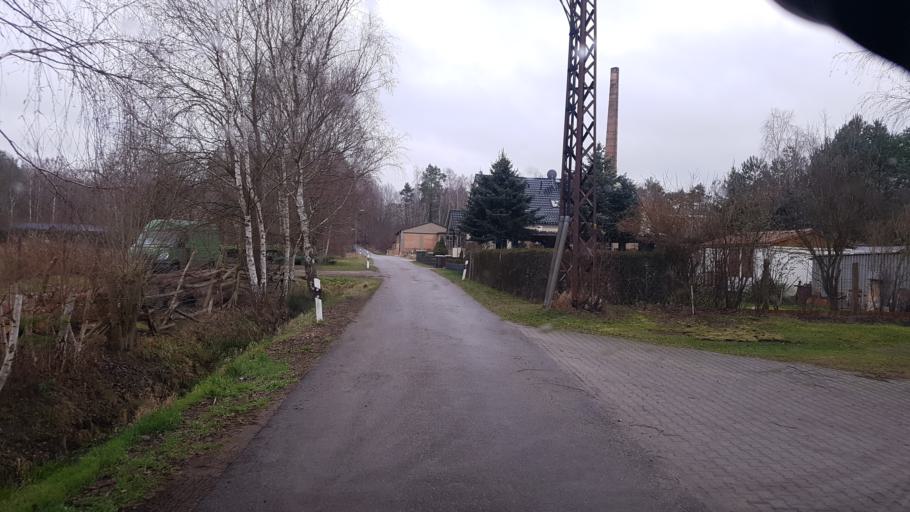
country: DE
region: Brandenburg
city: Crinitz
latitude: 51.7477
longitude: 13.7772
